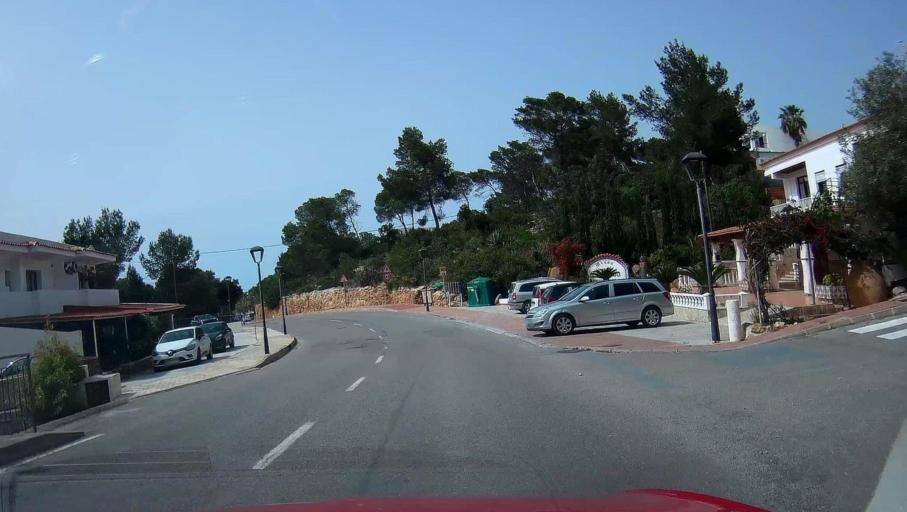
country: ES
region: Balearic Islands
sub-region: Illes Balears
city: Sant Joan de Labritja
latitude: 39.1084
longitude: 1.5199
